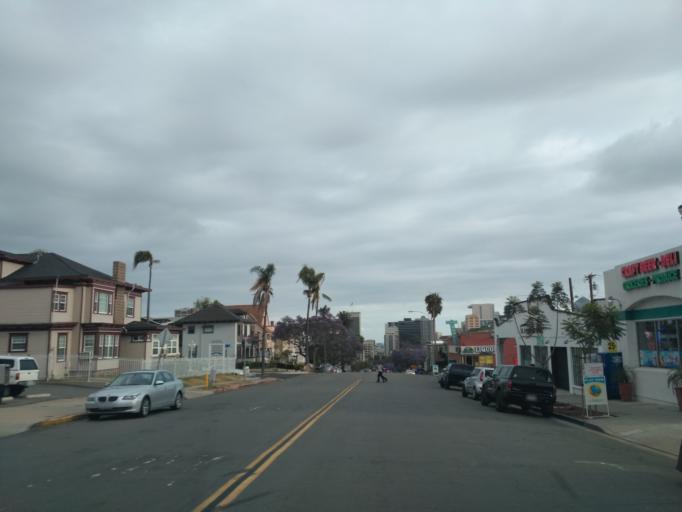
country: US
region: California
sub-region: San Diego County
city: San Diego
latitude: 32.7289
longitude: -117.1639
